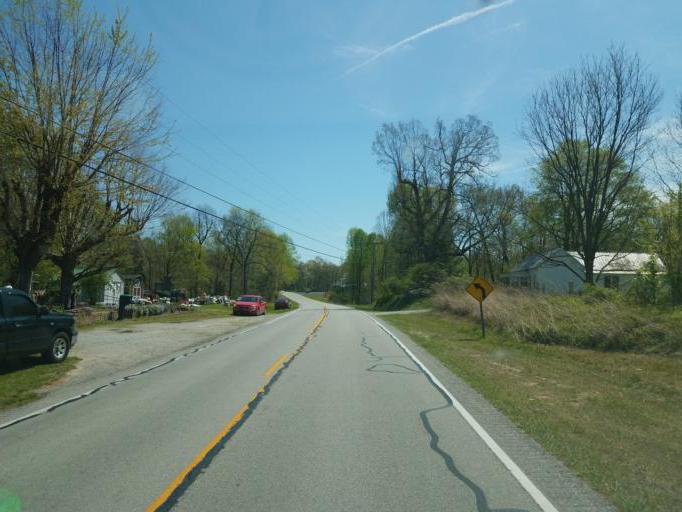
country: US
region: Kentucky
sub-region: Barren County
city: Cave City
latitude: 37.1320
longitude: -86.0311
